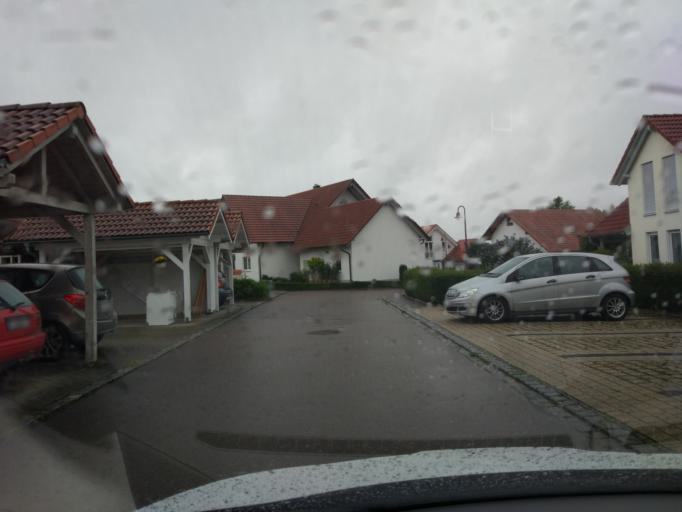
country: DE
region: Baden-Wuerttemberg
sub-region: Tuebingen Region
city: Huttisheim
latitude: 48.2805
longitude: 9.9384
